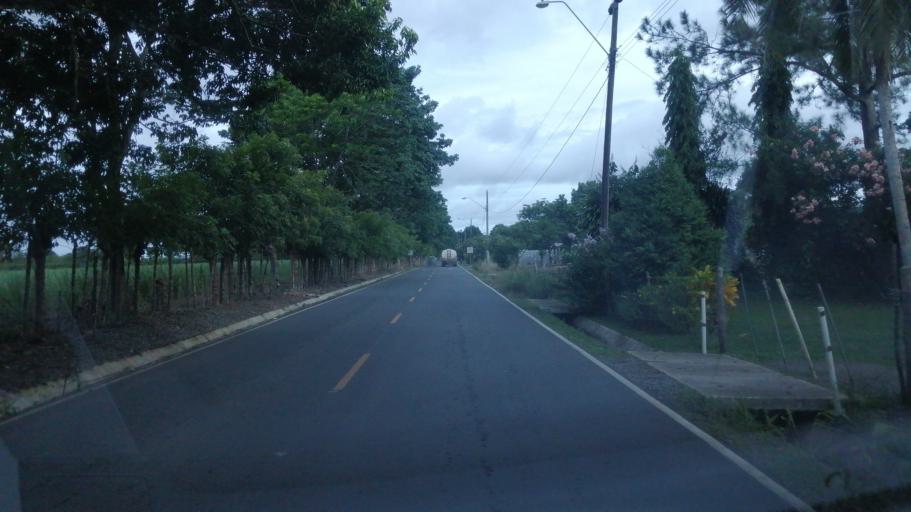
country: PA
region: Chiriqui
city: Alanje
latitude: 8.4154
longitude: -82.5189
